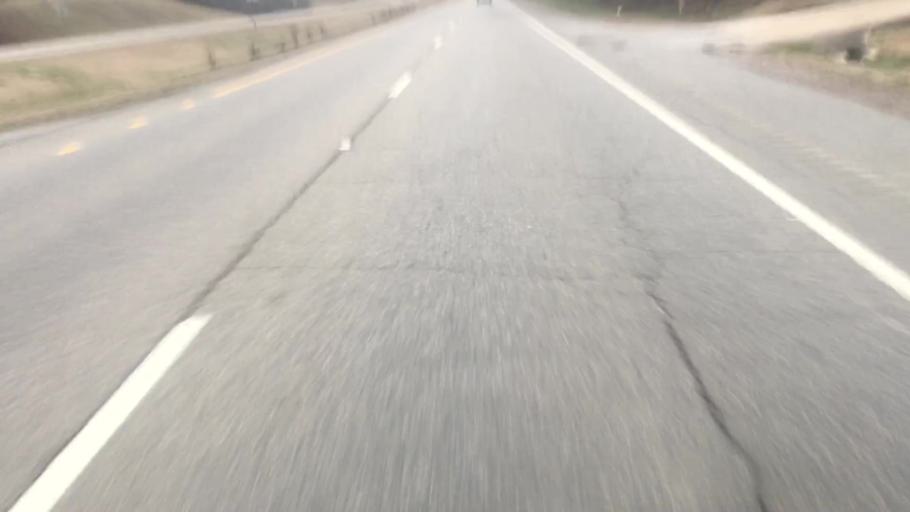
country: US
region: Alabama
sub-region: Walker County
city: Sumiton
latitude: 33.7401
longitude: -87.0334
